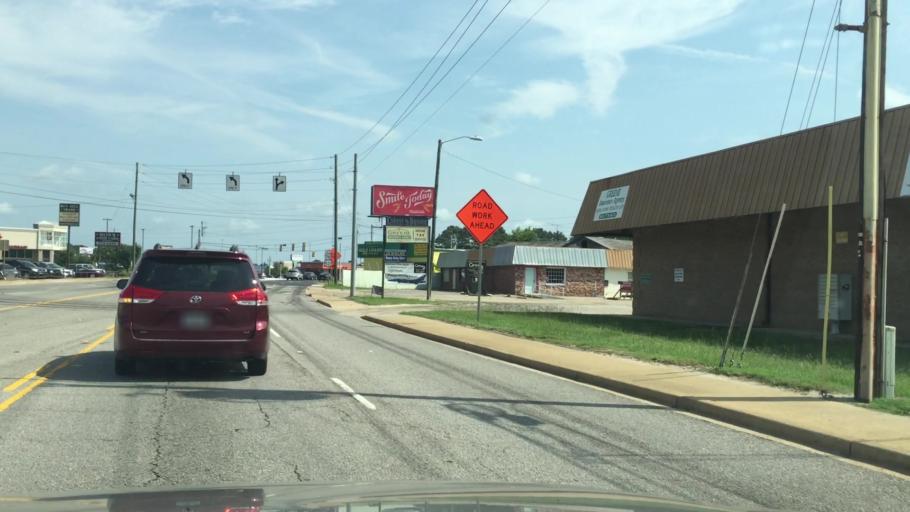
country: US
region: South Carolina
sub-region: Sumter County
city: Sumter
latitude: 33.9435
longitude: -80.3724
